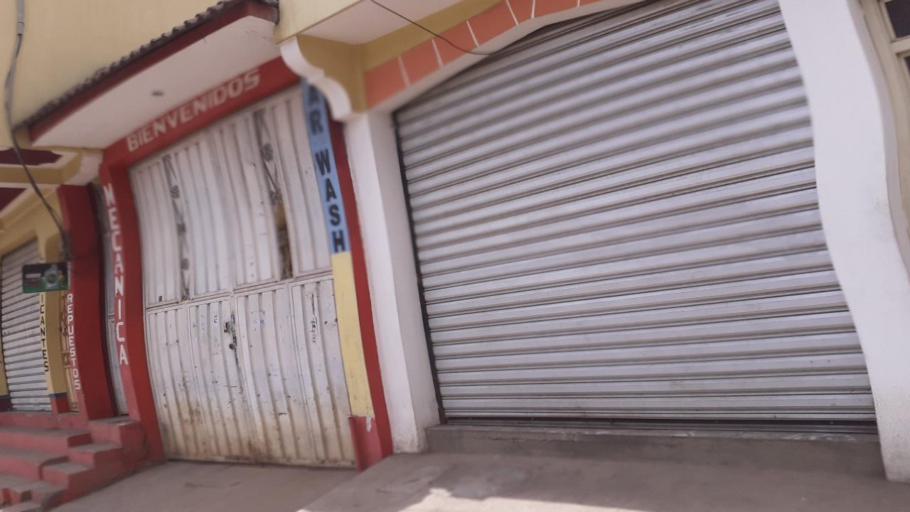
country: GT
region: Quetzaltenango
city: Ostuncalco
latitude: 14.8609
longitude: -91.6251
